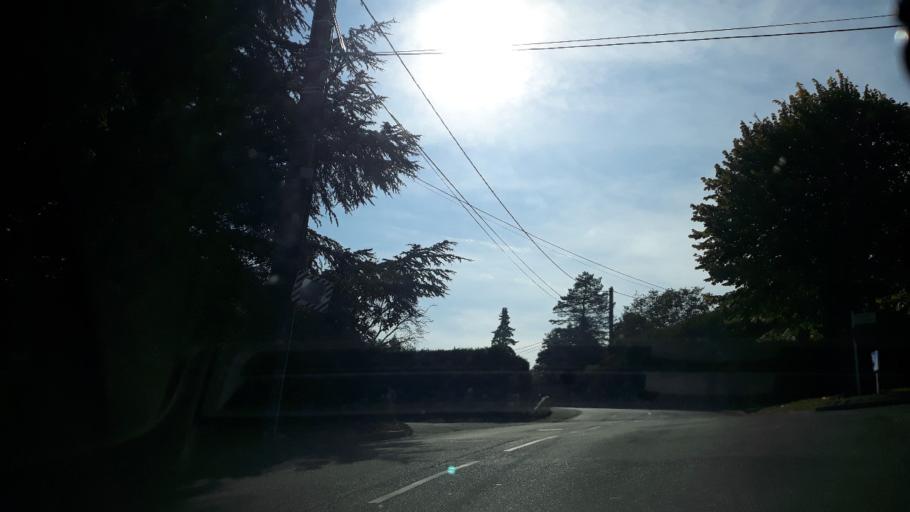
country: FR
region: Rhone-Alpes
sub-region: Departement du Rhone
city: Limas
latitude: 45.9722
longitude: 4.7082
